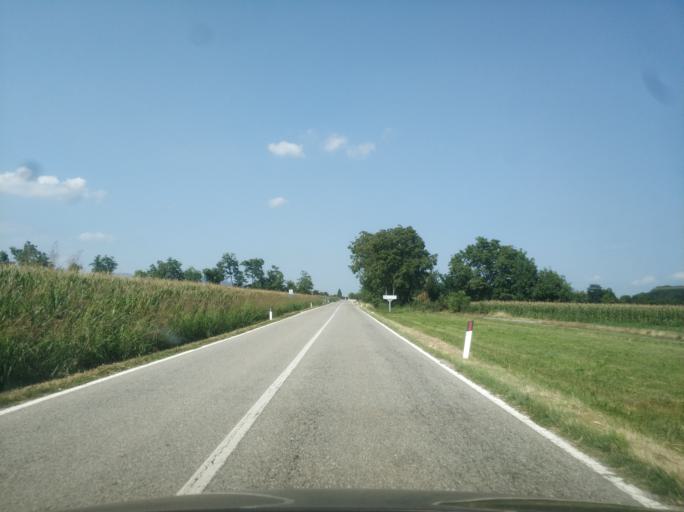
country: IT
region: Piedmont
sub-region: Provincia di Cuneo
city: Caraglio
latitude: 44.4430
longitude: 7.4535
